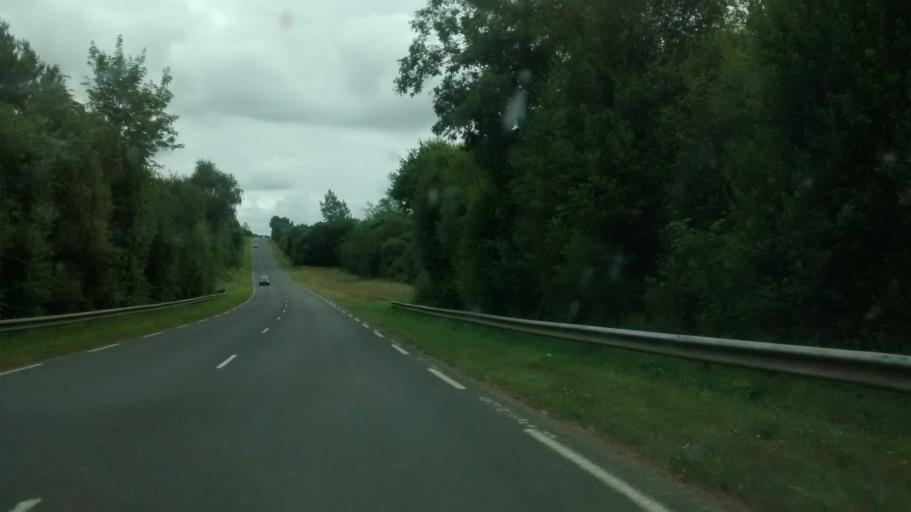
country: FR
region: Brittany
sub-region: Departement du Finistere
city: Le Folgoet
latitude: 48.5514
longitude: -4.3472
